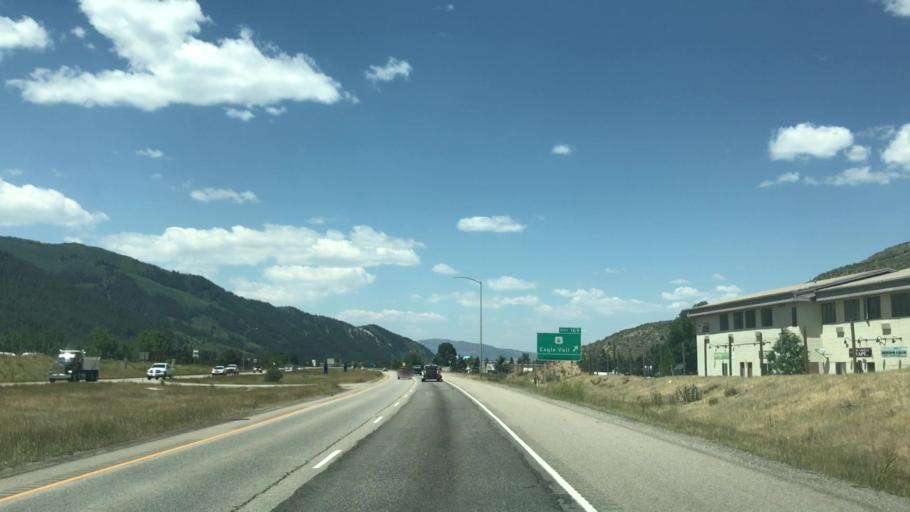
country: US
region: Colorado
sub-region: Eagle County
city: Avon
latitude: 39.6207
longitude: -106.4729
